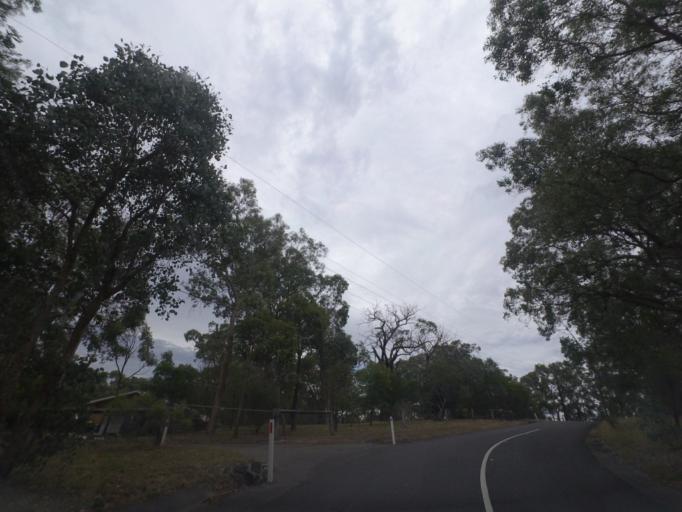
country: AU
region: Victoria
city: Plenty
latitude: -37.6608
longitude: 145.1322
